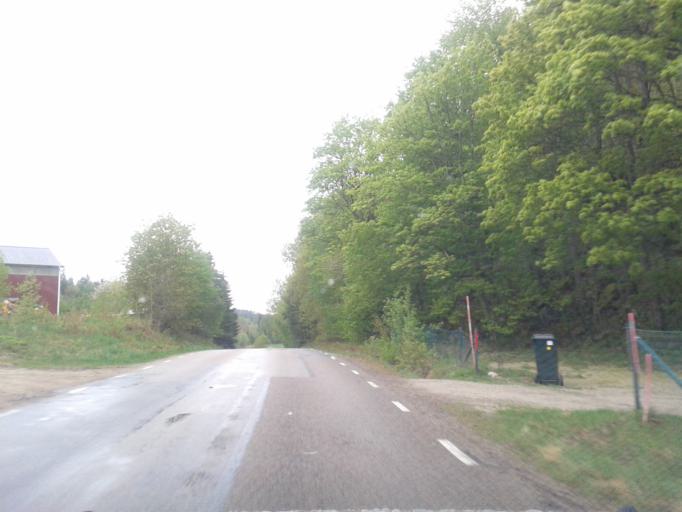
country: SE
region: Vaestra Goetaland
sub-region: Lilla Edets Kommun
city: Lodose
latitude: 58.0754
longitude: 11.9963
